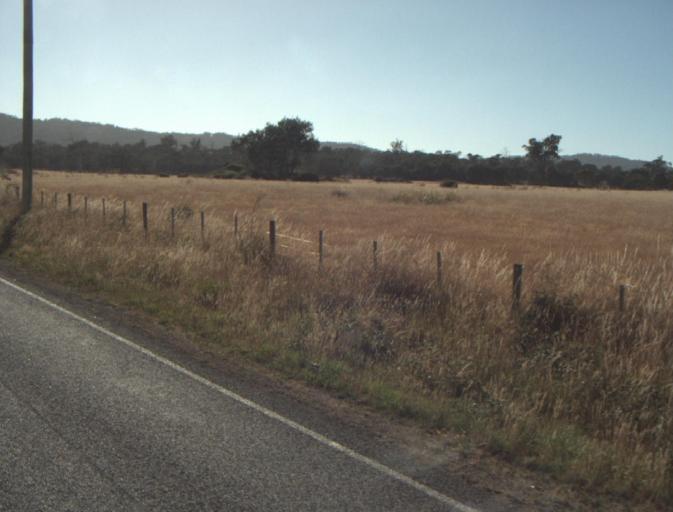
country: AU
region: Tasmania
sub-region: Launceston
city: Newstead
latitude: -41.4468
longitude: 147.2476
